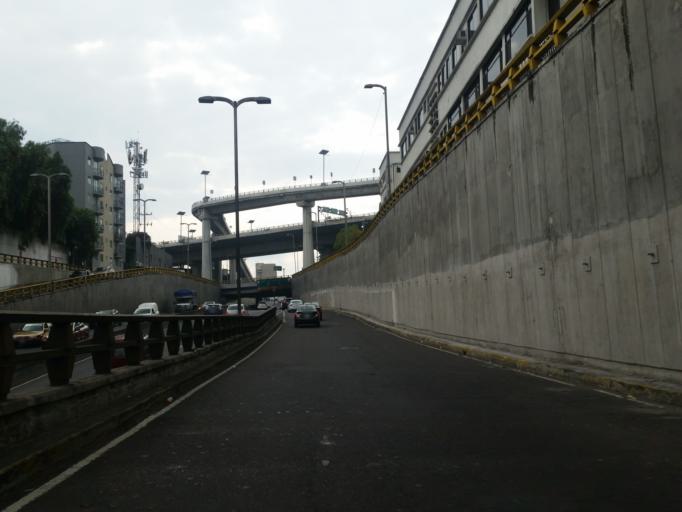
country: MX
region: Mexico City
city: Polanco
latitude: 19.4119
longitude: -99.1923
